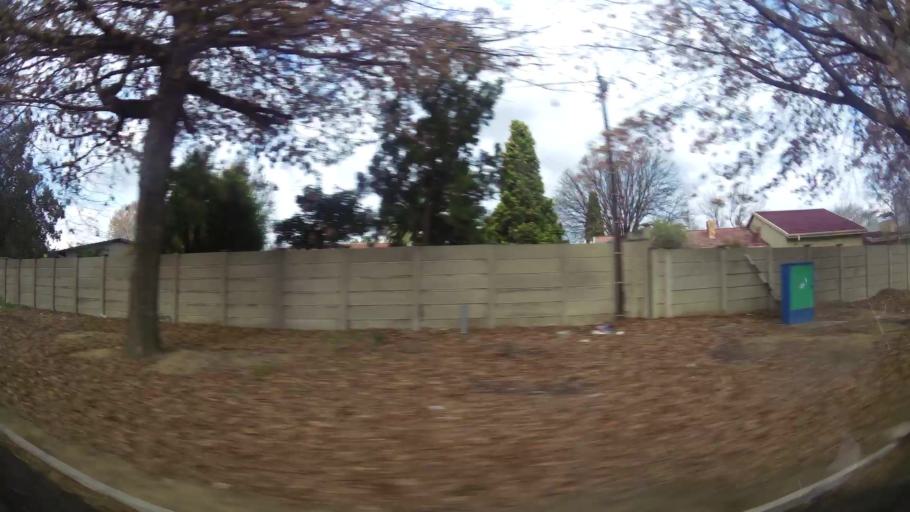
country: ZA
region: Orange Free State
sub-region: Fezile Dabi District Municipality
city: Sasolburg
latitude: -26.8014
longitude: 27.8184
